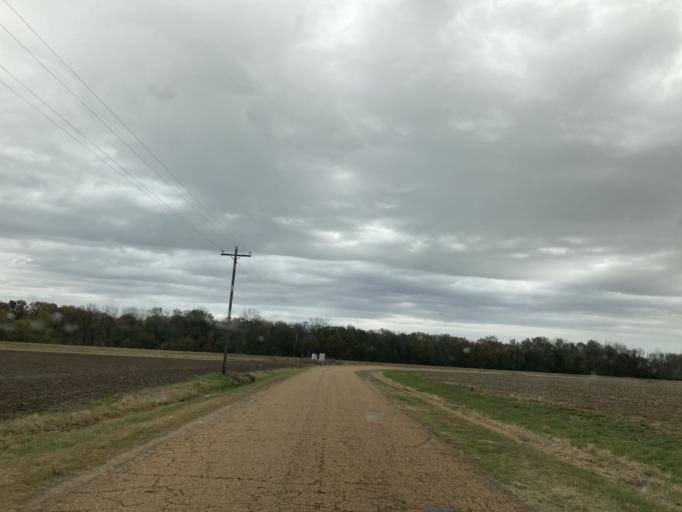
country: US
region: Mississippi
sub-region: Yazoo County
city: Yazoo City
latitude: 32.9824
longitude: -90.4223
